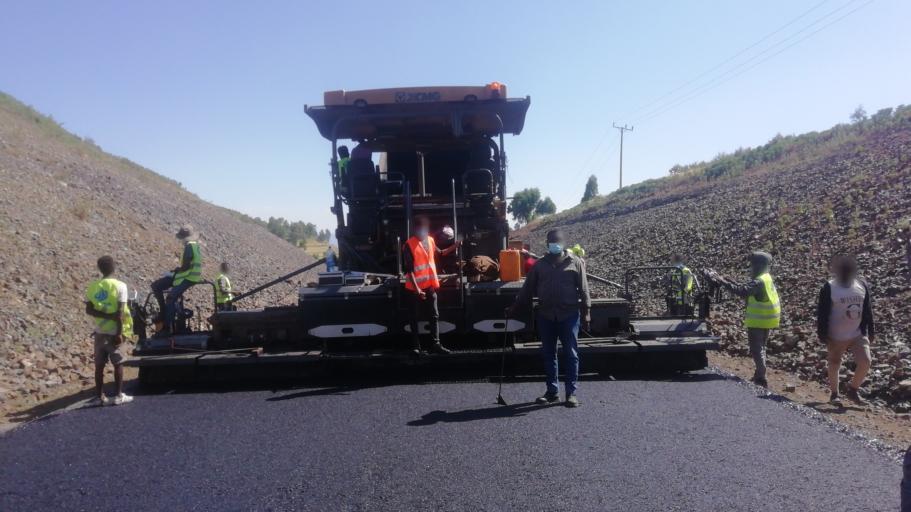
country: ET
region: Amhara
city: Addiet Canna
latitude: 11.3623
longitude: 37.8713
